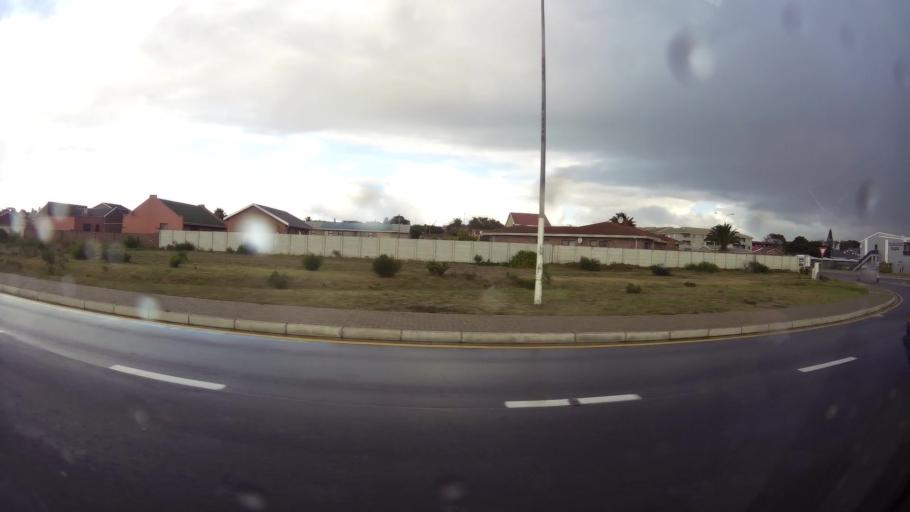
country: ZA
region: Western Cape
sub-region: Eden District Municipality
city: Mossel Bay
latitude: -34.1831
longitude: 22.1027
